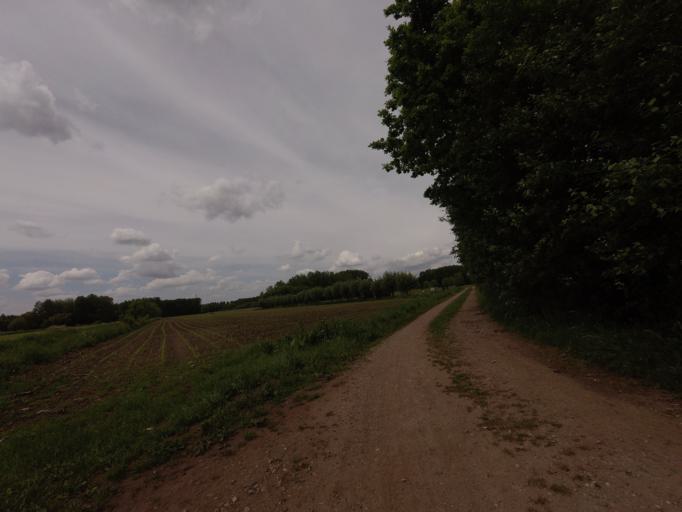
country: BE
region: Flanders
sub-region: Provincie Antwerpen
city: Bornem
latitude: 51.1024
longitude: 4.2544
